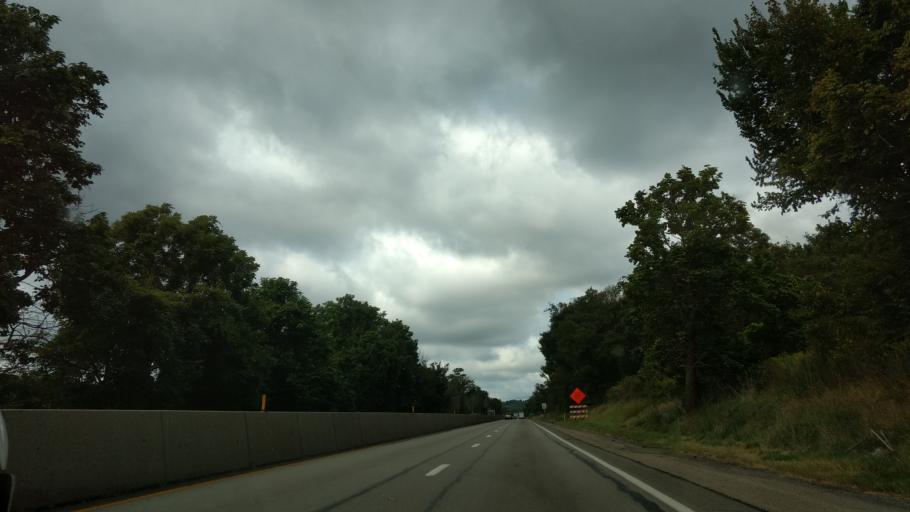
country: US
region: Pennsylvania
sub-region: Westmoreland County
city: Fellsburg
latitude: 40.1537
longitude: -79.7819
